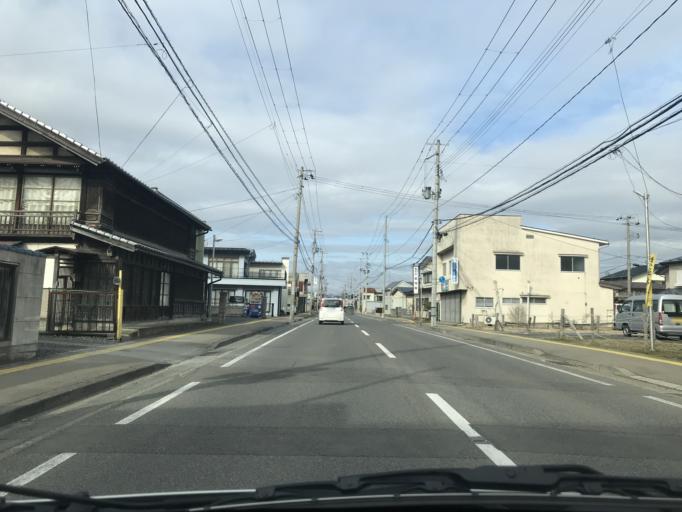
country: JP
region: Iwate
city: Hanamaki
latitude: 39.3980
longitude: 141.1175
